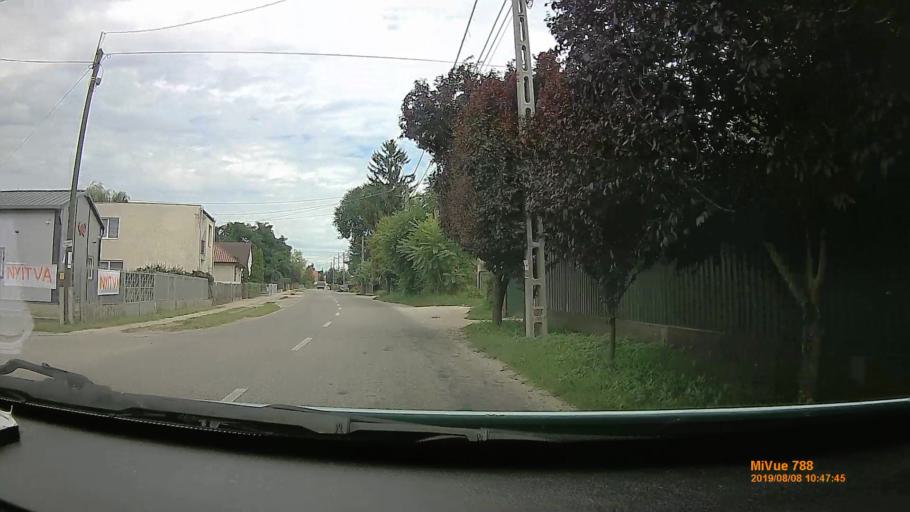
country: HU
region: Szabolcs-Szatmar-Bereg
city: Balkany
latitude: 47.7636
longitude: 21.8630
